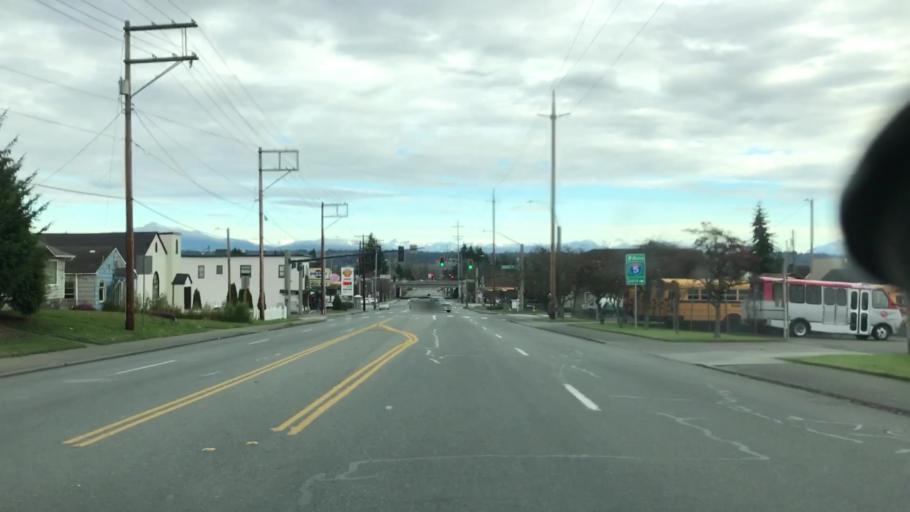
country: US
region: Washington
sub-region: Snohomish County
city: Everett
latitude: 47.9818
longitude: -122.1923
